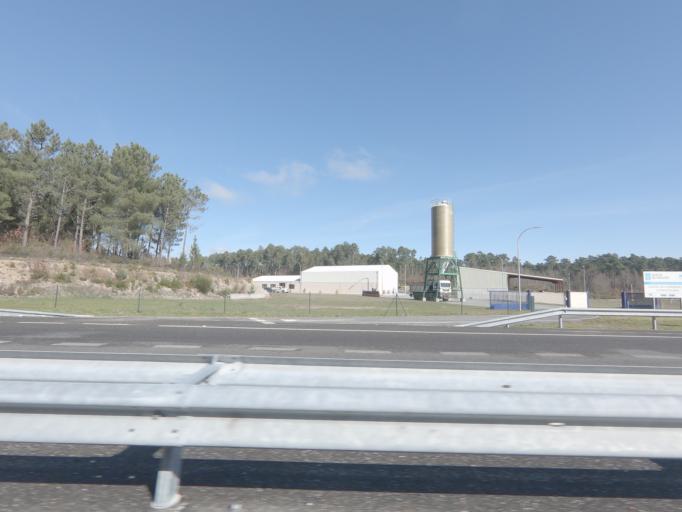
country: ES
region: Galicia
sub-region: Provincia de Ourense
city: Maside
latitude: 42.4509
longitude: -8.0264
